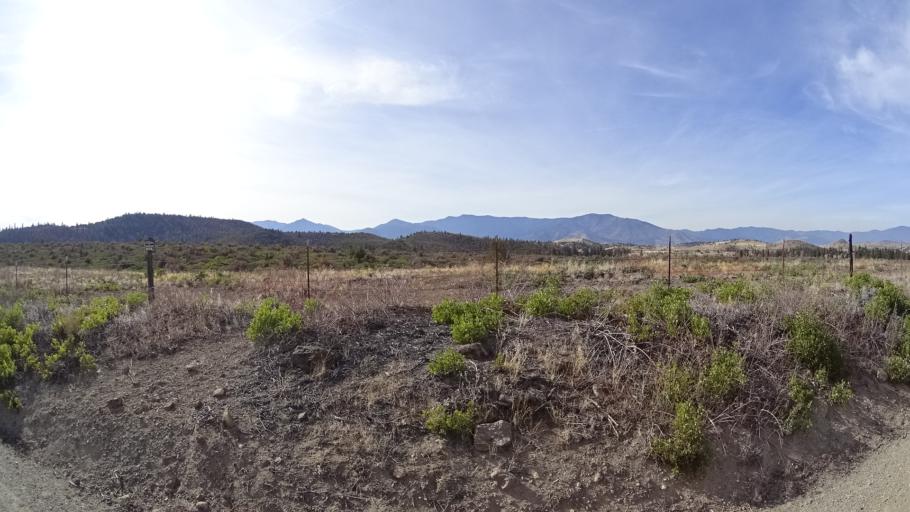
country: US
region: California
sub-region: Siskiyou County
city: Weed
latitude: 41.4845
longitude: -122.3660
